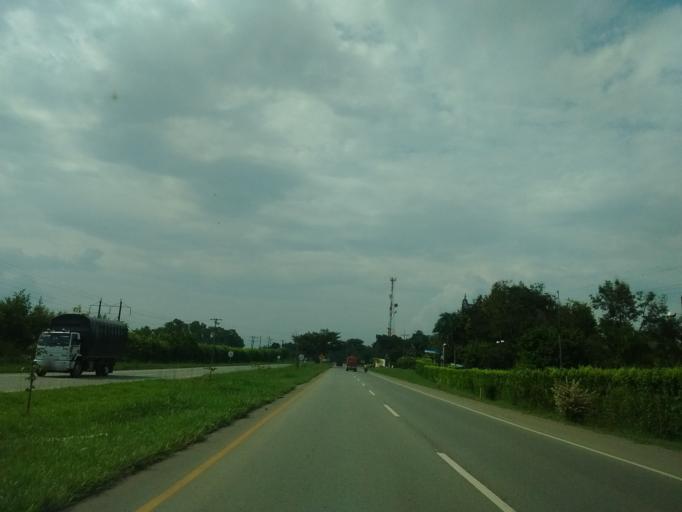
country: CO
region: Cauca
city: Santander de Quilichao
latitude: 3.0823
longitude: -76.4739
